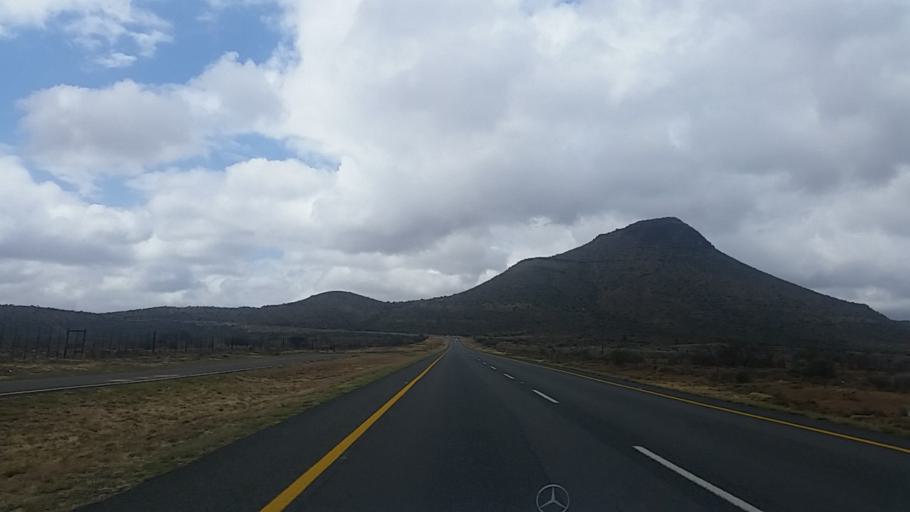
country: ZA
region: Eastern Cape
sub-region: Cacadu District Municipality
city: Graaff-Reinet
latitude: -32.1232
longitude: 24.5996
